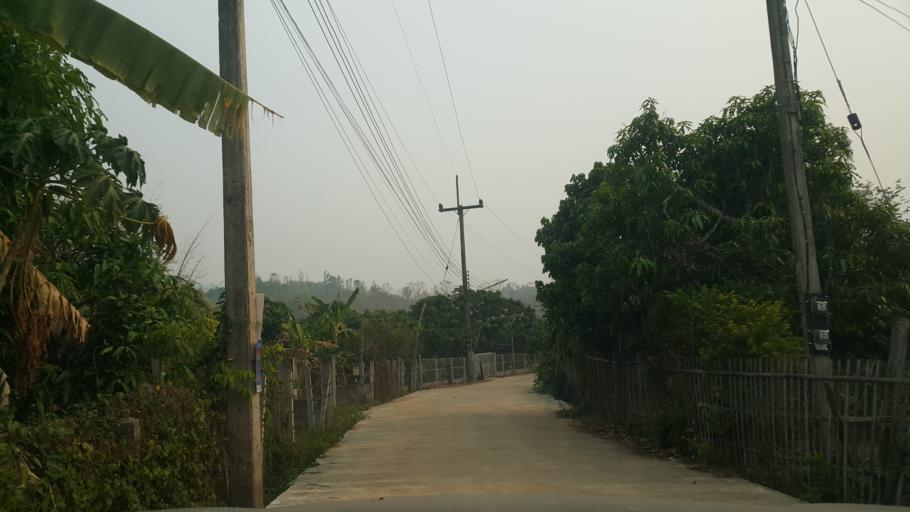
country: TH
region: Lamphun
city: Mae Tha
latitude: 18.5103
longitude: 99.2135
